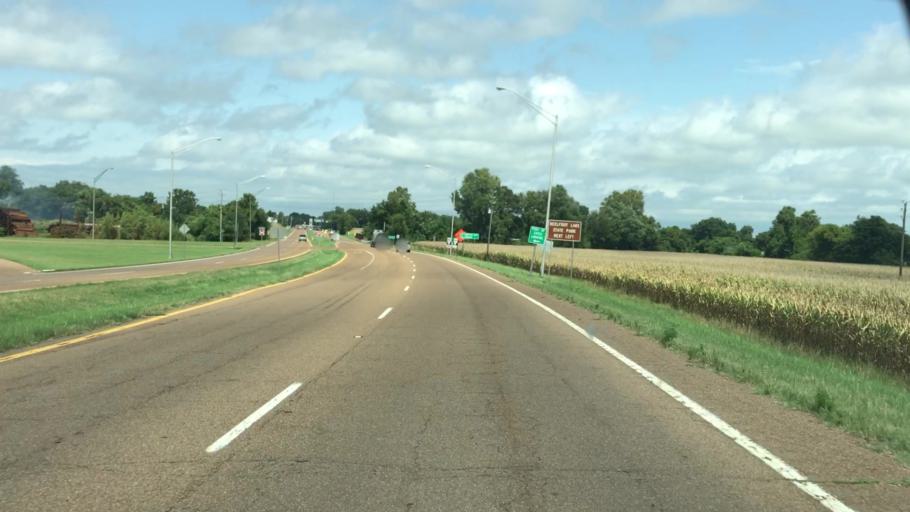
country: US
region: Tennessee
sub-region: Obion County
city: Troy
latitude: 36.3370
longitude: -89.1579
